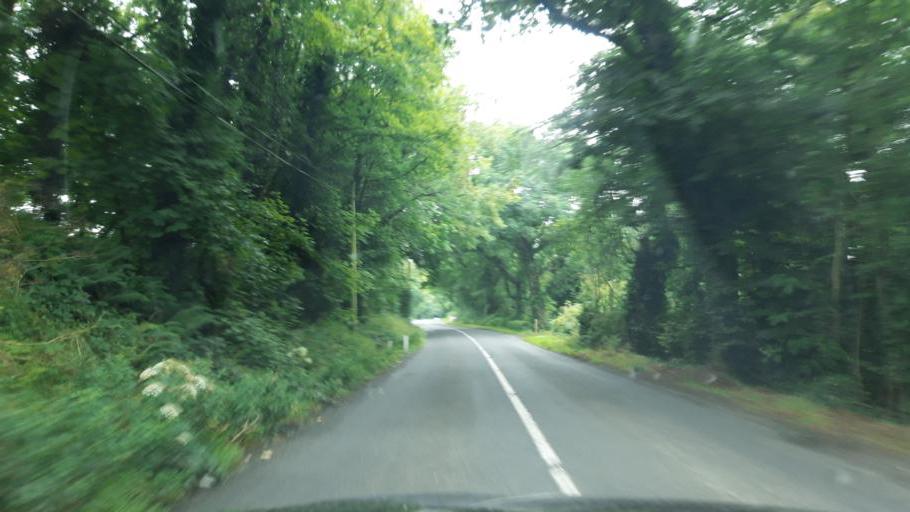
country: IE
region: Munster
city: Fethard
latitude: 52.5407
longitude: -7.6815
